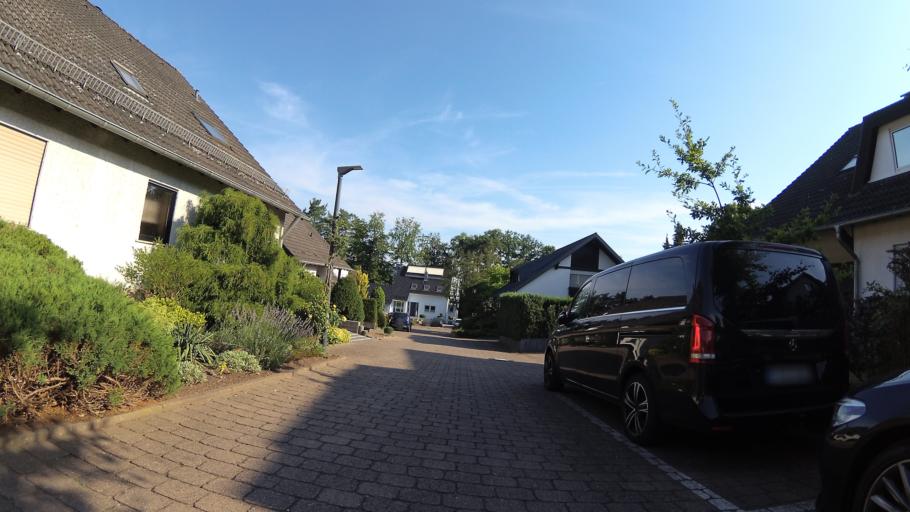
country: DE
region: Saarland
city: Homburg
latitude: 49.3409
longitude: 7.3180
